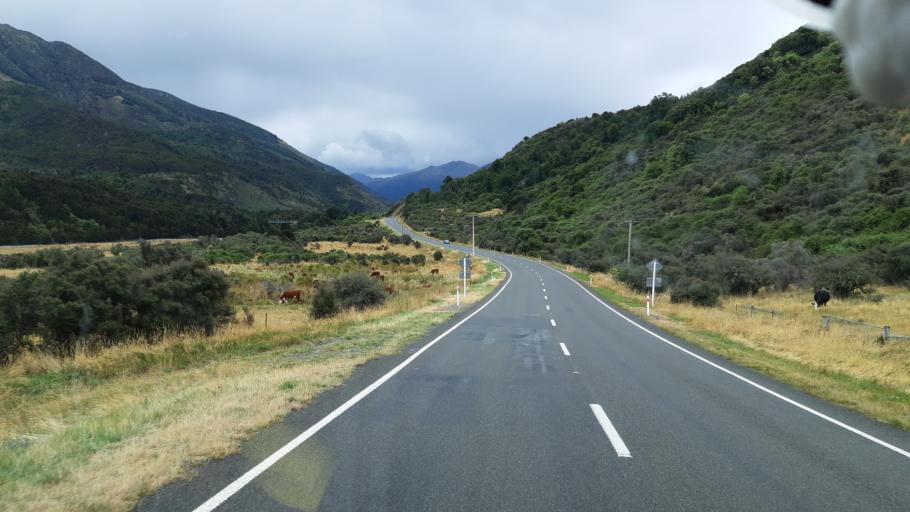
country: NZ
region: Canterbury
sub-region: Hurunui District
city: Amberley
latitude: -42.5741
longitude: 172.3719
